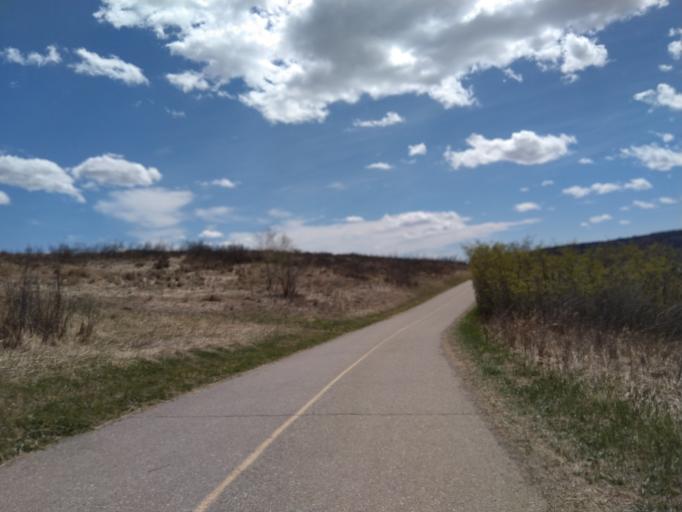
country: CA
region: Alberta
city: Calgary
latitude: 51.0963
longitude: -114.1860
